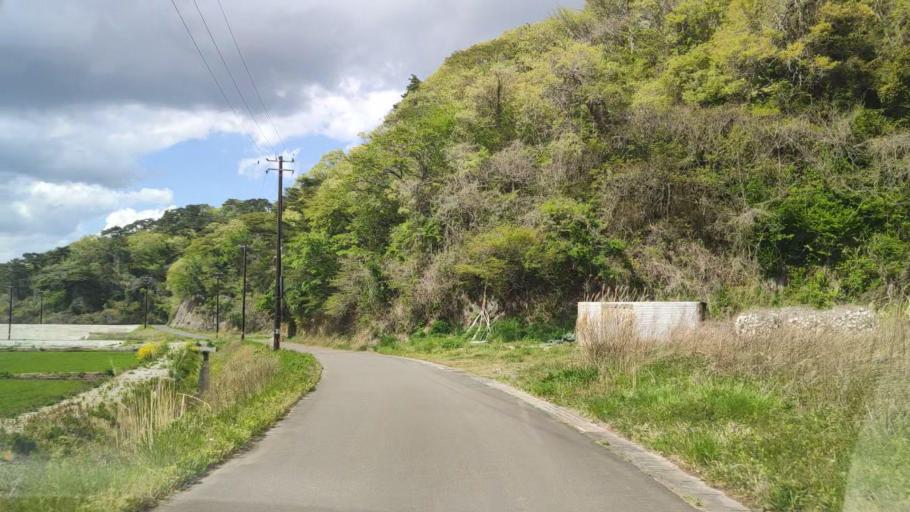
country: JP
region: Miyagi
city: Yamoto
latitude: 38.3391
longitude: 141.1644
